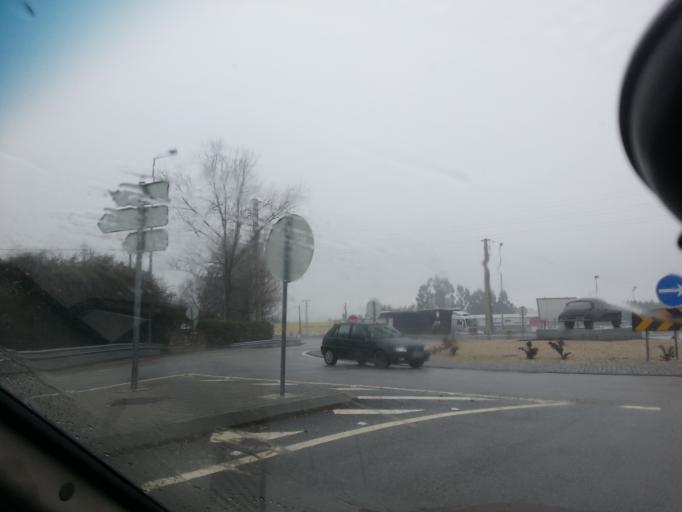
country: PT
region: Viseu
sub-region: Mangualde
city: Mangualde
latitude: 40.6093
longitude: -7.7782
